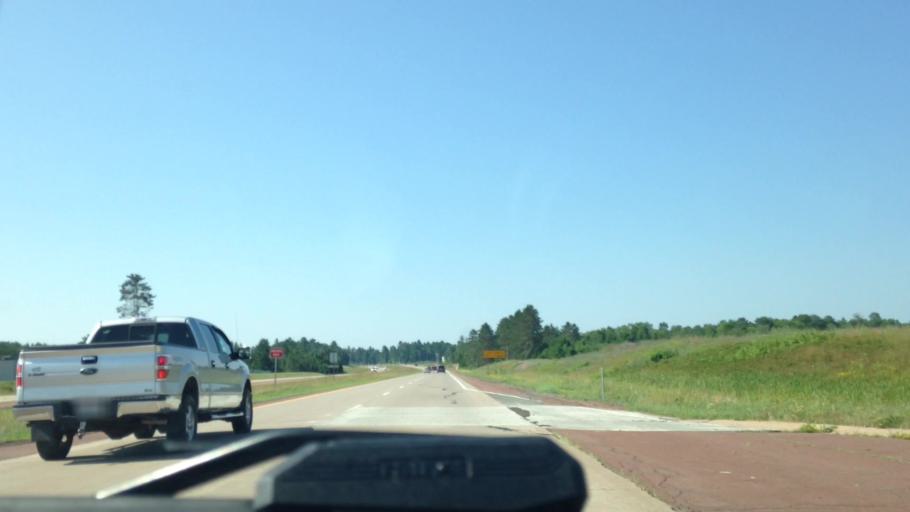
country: US
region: Wisconsin
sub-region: Douglas County
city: Lake Nebagamon
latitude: 46.3600
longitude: -91.8325
